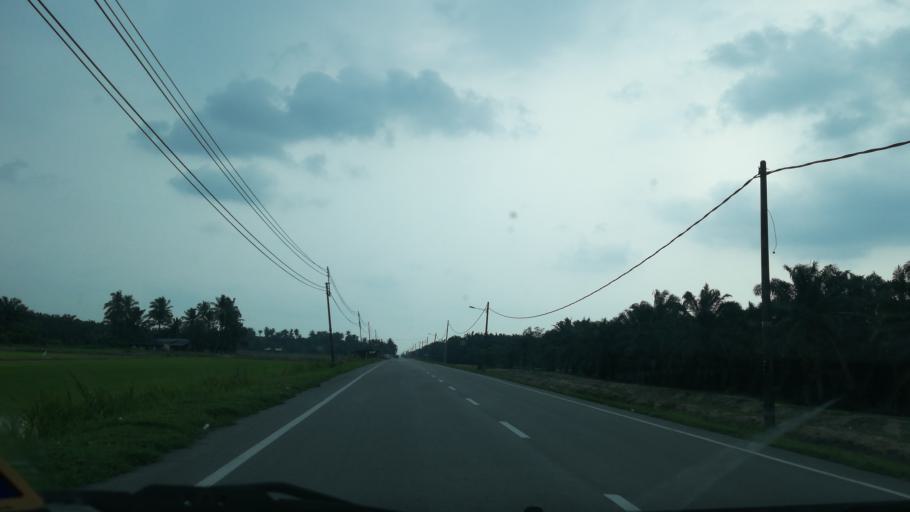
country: MY
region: Perak
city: Teluk Intan
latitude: 4.1185
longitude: 101.0765
